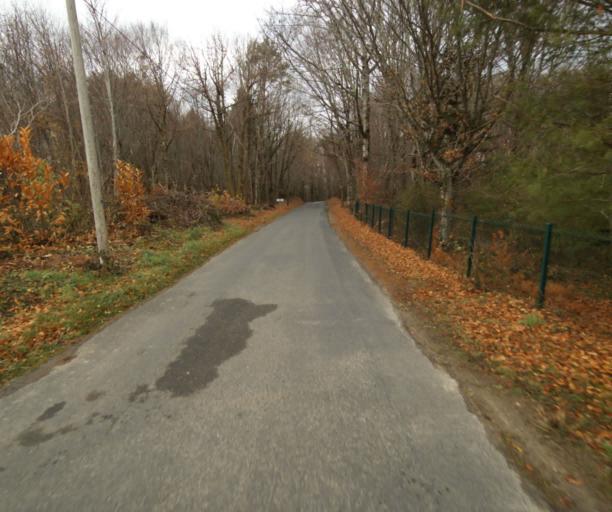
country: FR
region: Limousin
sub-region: Departement de la Correze
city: Laguenne
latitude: 45.2313
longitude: 1.7617
